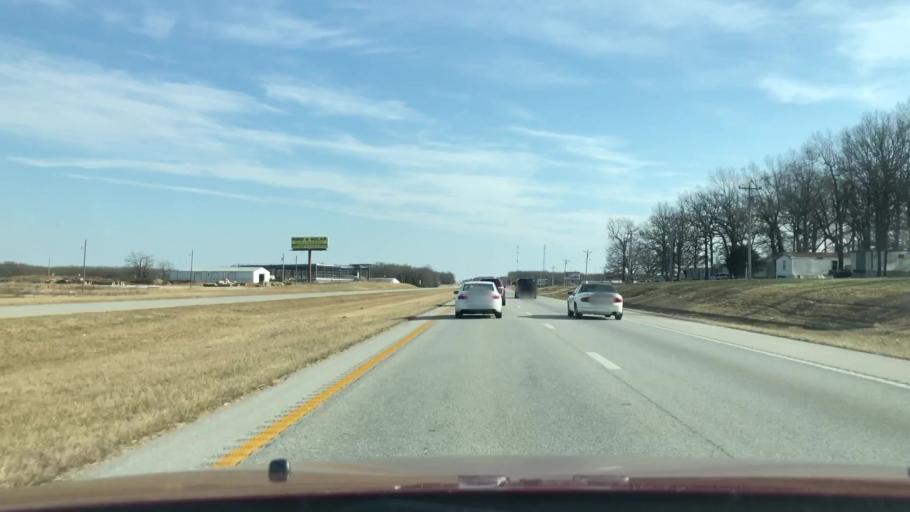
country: US
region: Missouri
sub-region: Webster County
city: Rogersville
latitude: 37.1146
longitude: -93.0344
